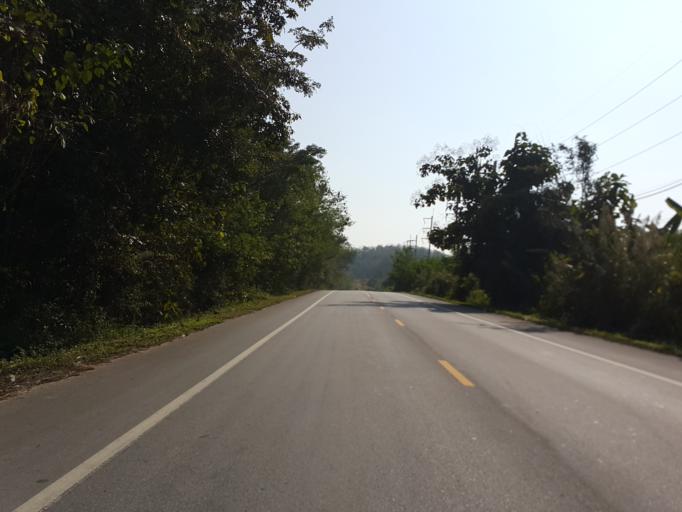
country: TH
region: Lampang
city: Chae Hom
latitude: 18.6191
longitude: 99.5436
